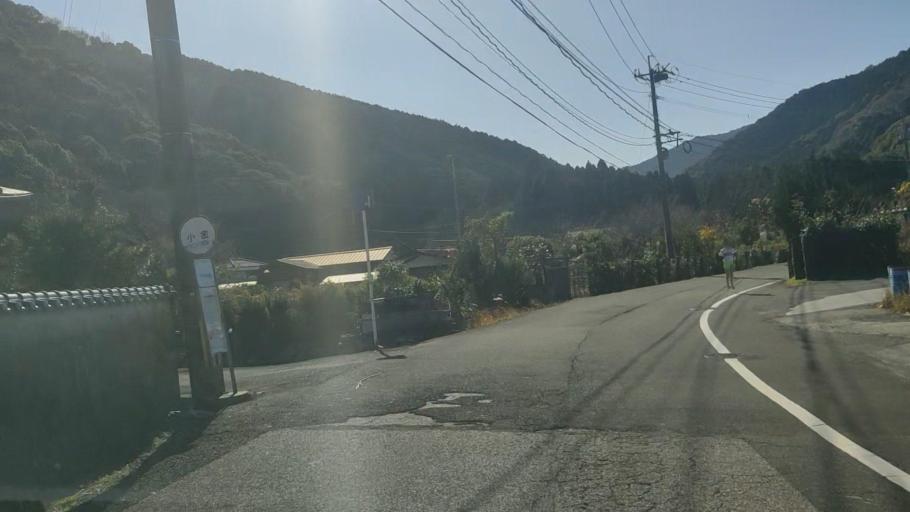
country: JP
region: Oita
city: Saiki
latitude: 32.8353
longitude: 131.9535
